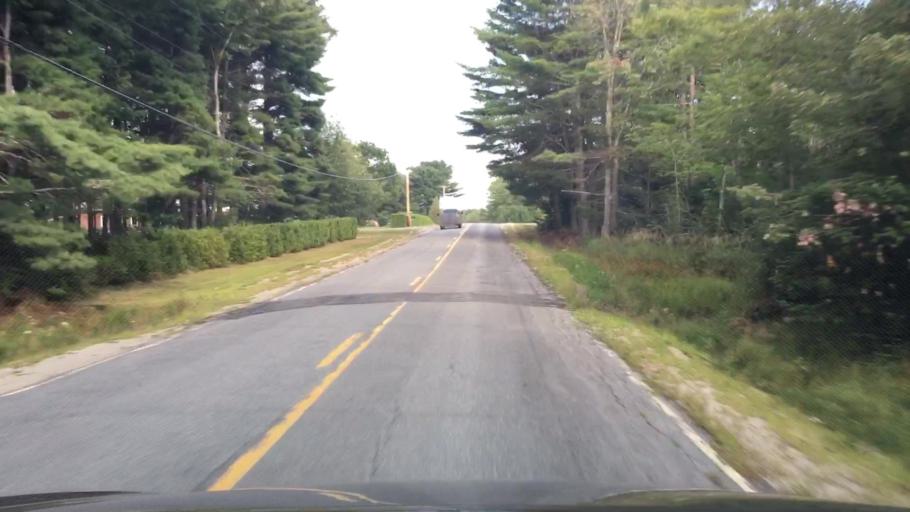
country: US
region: Maine
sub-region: Hancock County
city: Surry
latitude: 44.4996
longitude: -68.5543
